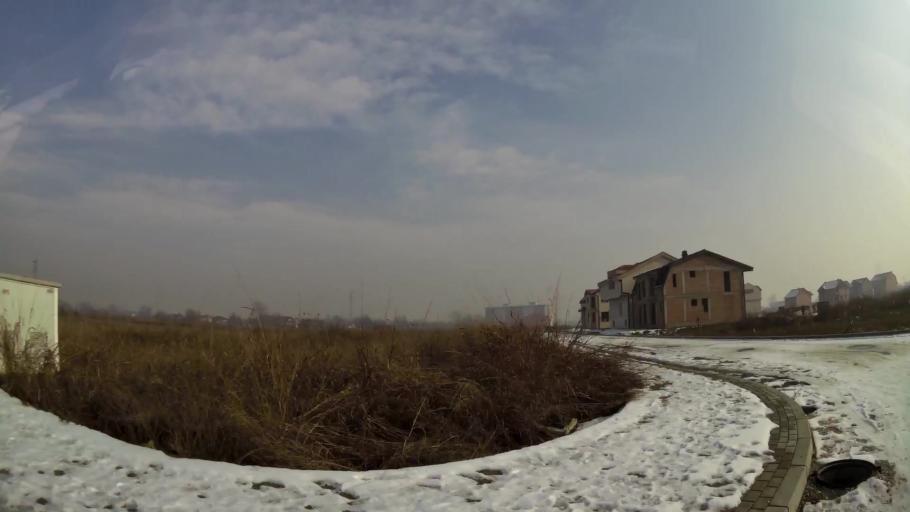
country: MK
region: Kisela Voda
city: Kisela Voda
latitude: 41.9938
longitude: 21.5145
